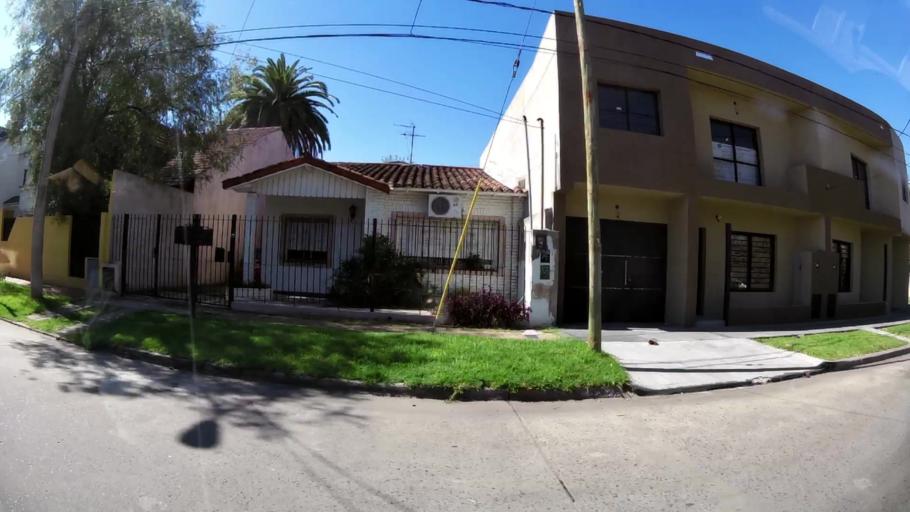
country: AR
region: Buenos Aires
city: Ituzaingo
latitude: -34.6331
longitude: -58.6554
